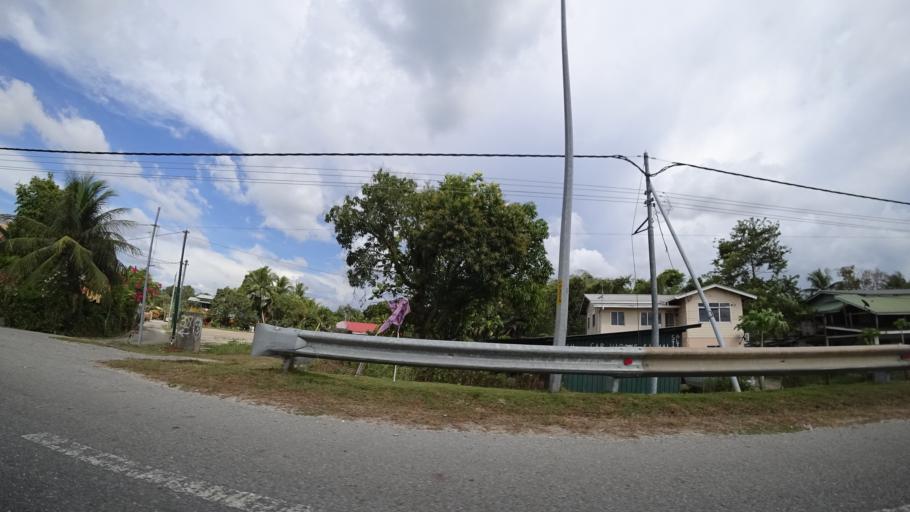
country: BN
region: Brunei and Muara
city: Bandar Seri Begawan
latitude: 4.8267
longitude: 114.8642
